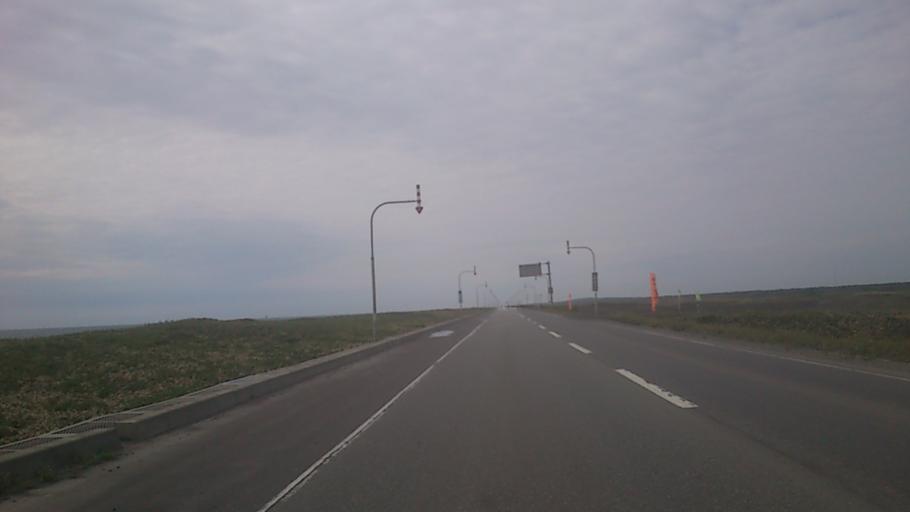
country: JP
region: Hokkaido
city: Makubetsu
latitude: 45.0080
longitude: 141.6781
